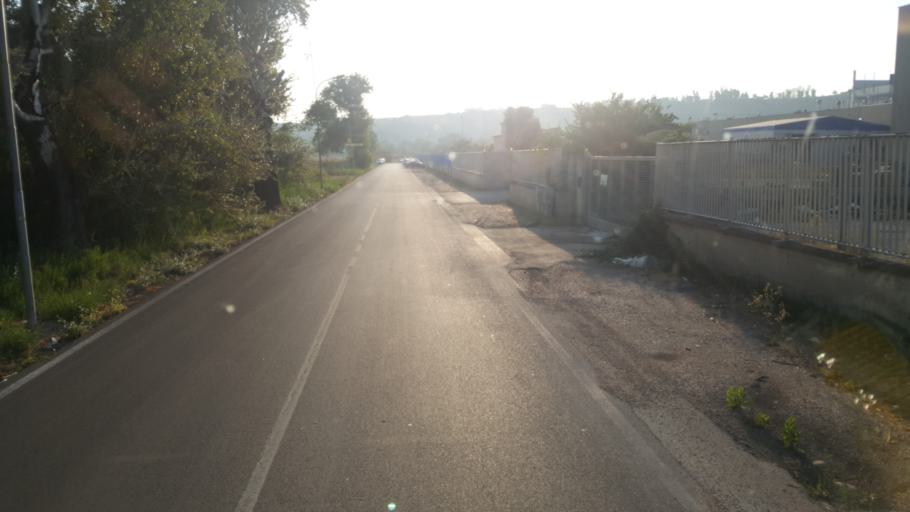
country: IT
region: Molise
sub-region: Provincia di Campobasso
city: Portocannone
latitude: 41.9459
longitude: 15.0036
